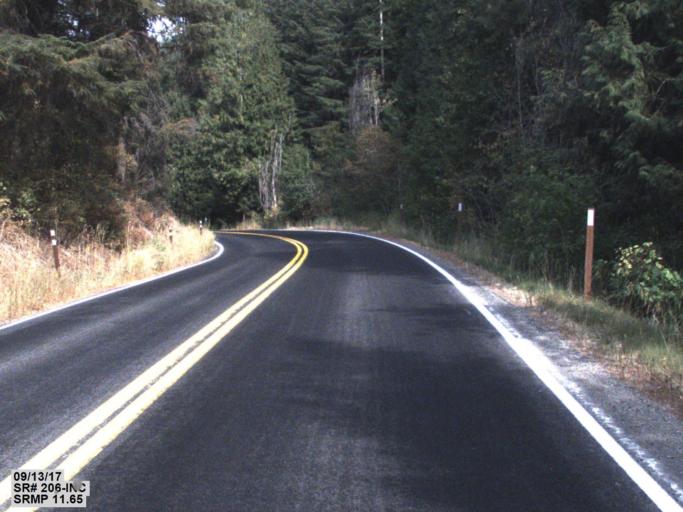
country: US
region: Washington
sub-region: Spokane County
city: Trentwood
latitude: 47.8451
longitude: -117.1711
